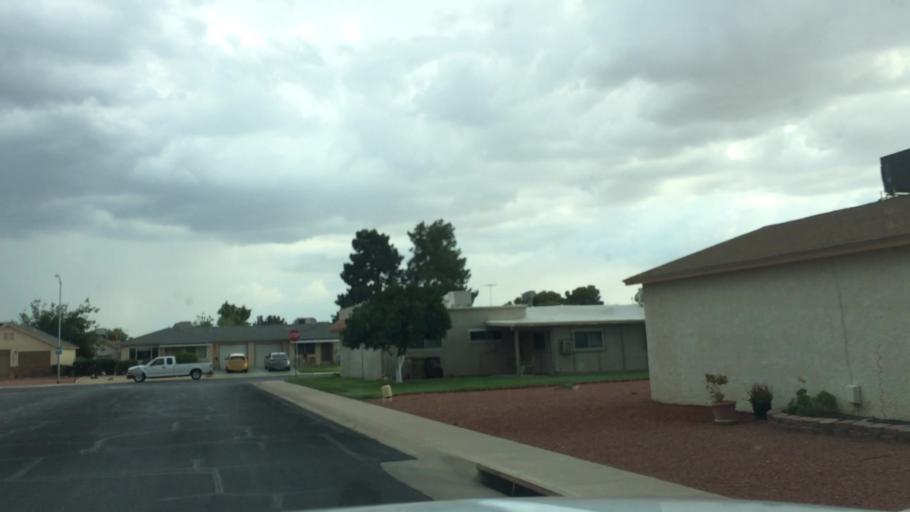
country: US
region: Arizona
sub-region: Maricopa County
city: Sun City
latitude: 33.5796
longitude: -112.2653
